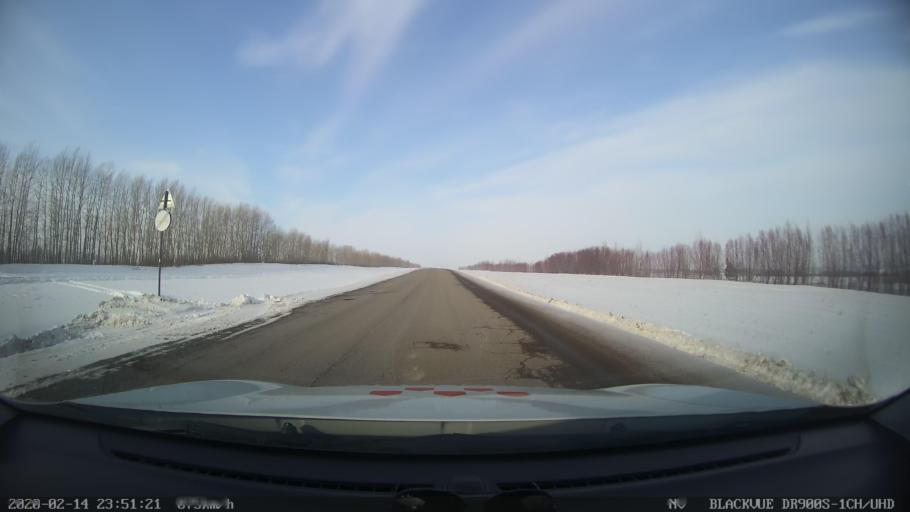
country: RU
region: Tatarstan
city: Kuybyshevskiy Zaton
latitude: 55.2655
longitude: 49.1465
